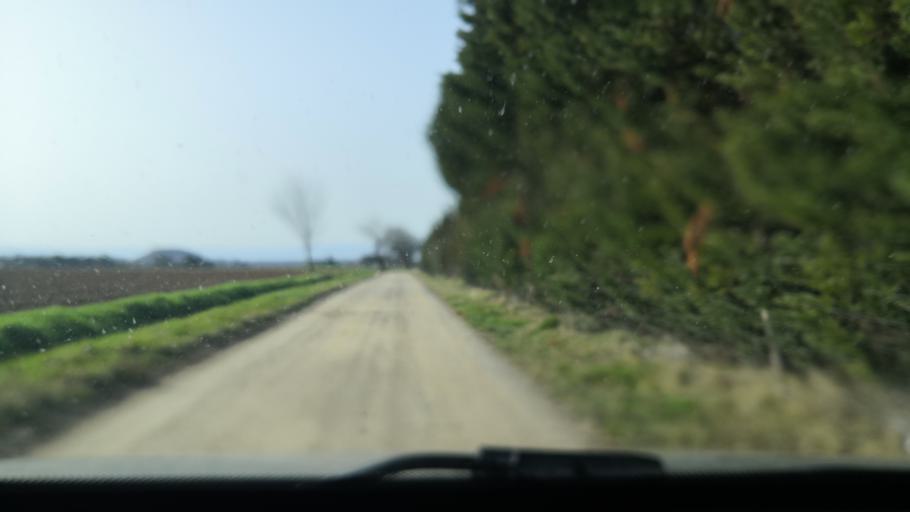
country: FR
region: Rhone-Alpes
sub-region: Departement de la Drome
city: La Begude-de-Mazenc
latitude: 44.5543
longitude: 4.9013
